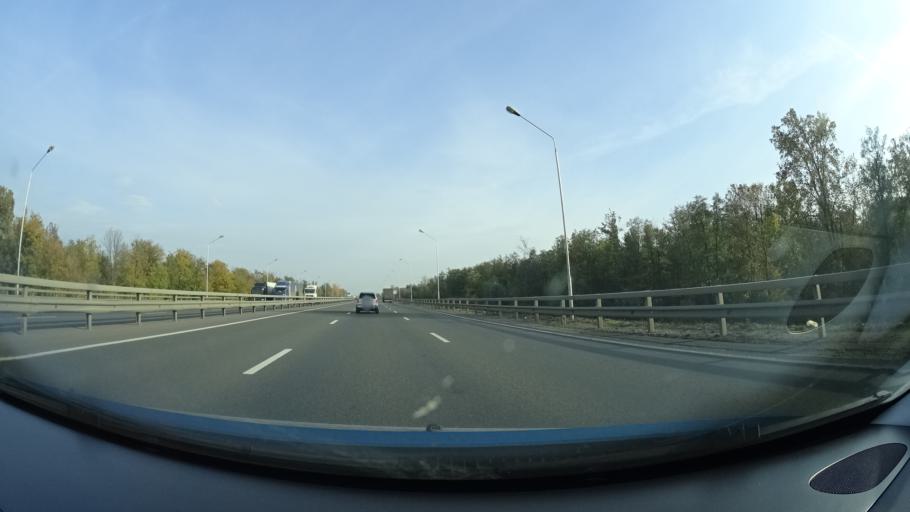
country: RU
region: Bashkortostan
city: Ufa
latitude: 54.6543
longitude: 55.8987
